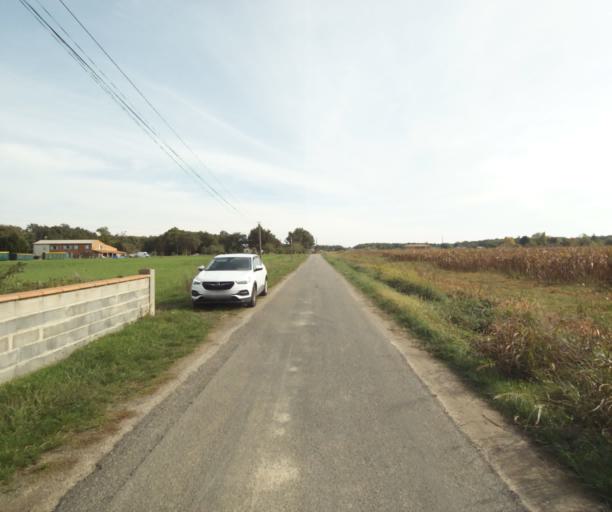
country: FR
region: Midi-Pyrenees
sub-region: Departement du Tarn-et-Garonne
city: Labastide-Saint-Pierre
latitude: 43.9152
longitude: 1.3842
